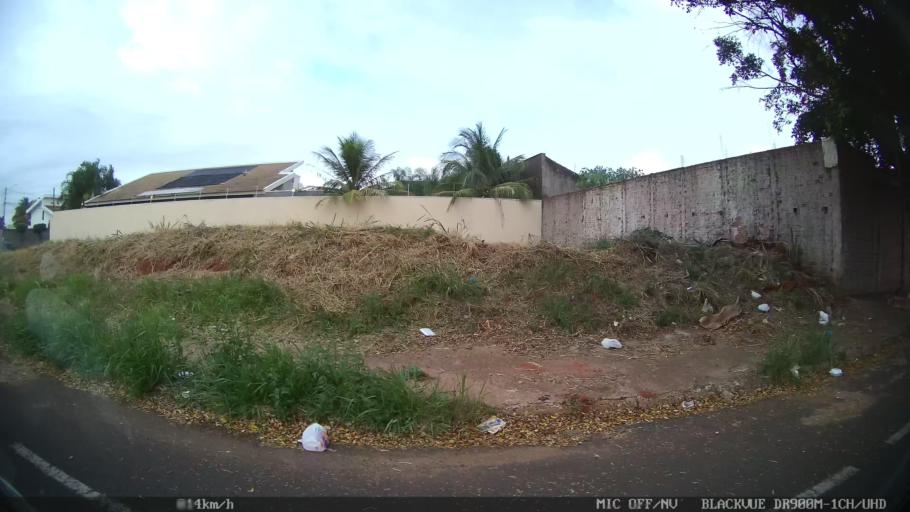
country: BR
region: Sao Paulo
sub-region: Sao Jose Do Rio Preto
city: Sao Jose do Rio Preto
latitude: -20.8405
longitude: -49.4001
